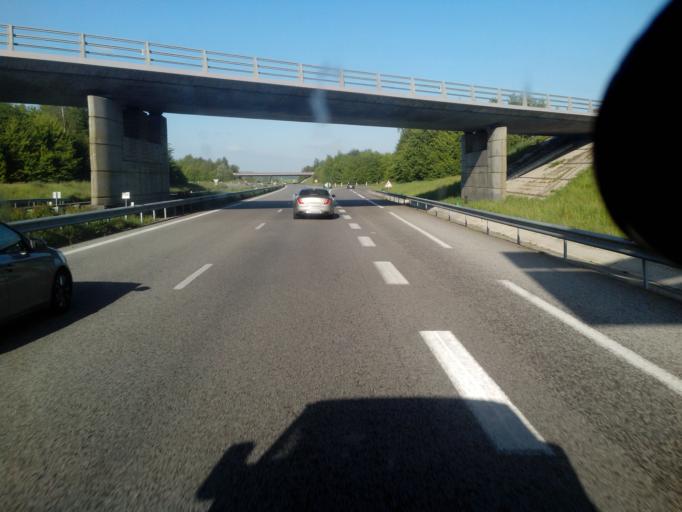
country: FR
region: Haute-Normandie
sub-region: Departement de la Seine-Maritime
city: Valliquerville
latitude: 49.6299
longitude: 0.6400
